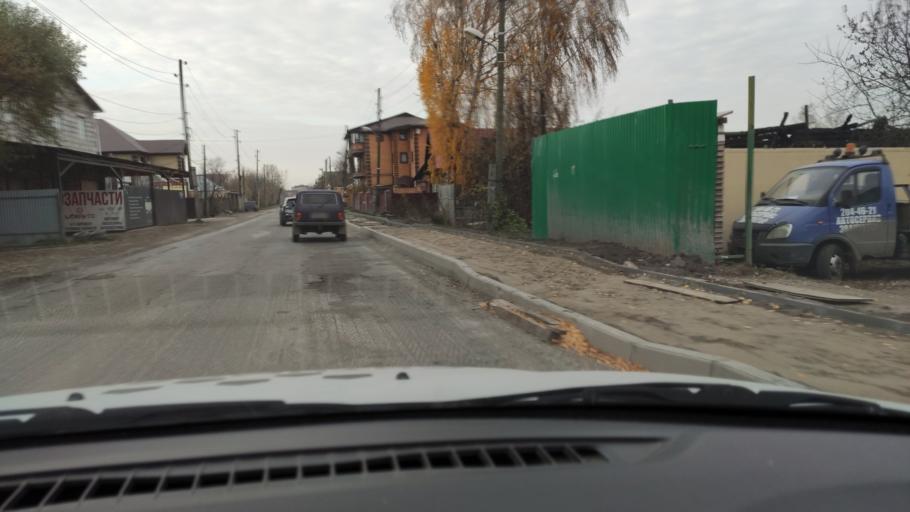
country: RU
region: Perm
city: Kondratovo
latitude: 57.9647
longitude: 56.1201
